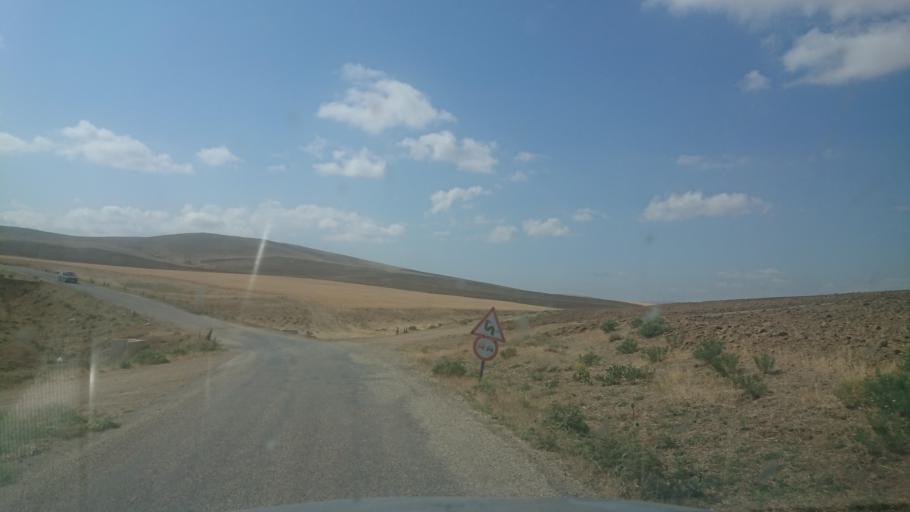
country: TR
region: Aksaray
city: Sariyahsi
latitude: 39.0084
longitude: 33.9498
